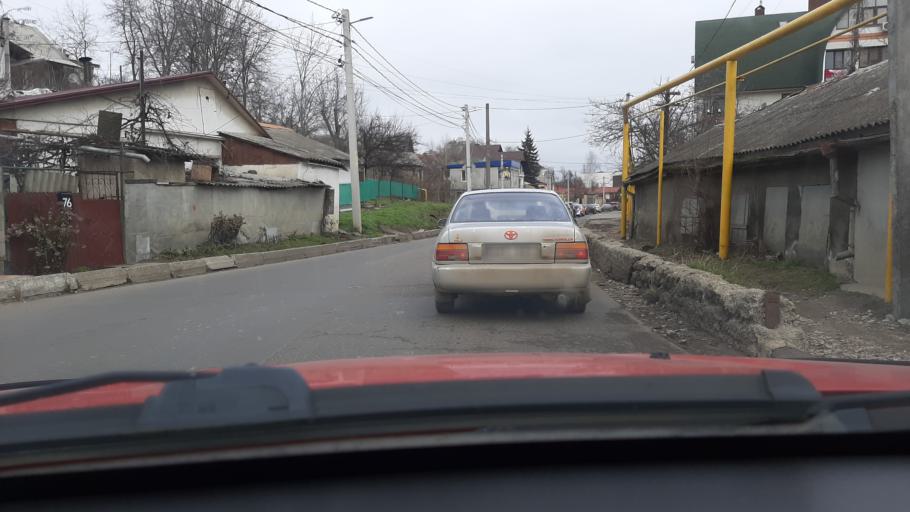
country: MD
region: Chisinau
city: Chisinau
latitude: 47.0055
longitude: 28.8372
